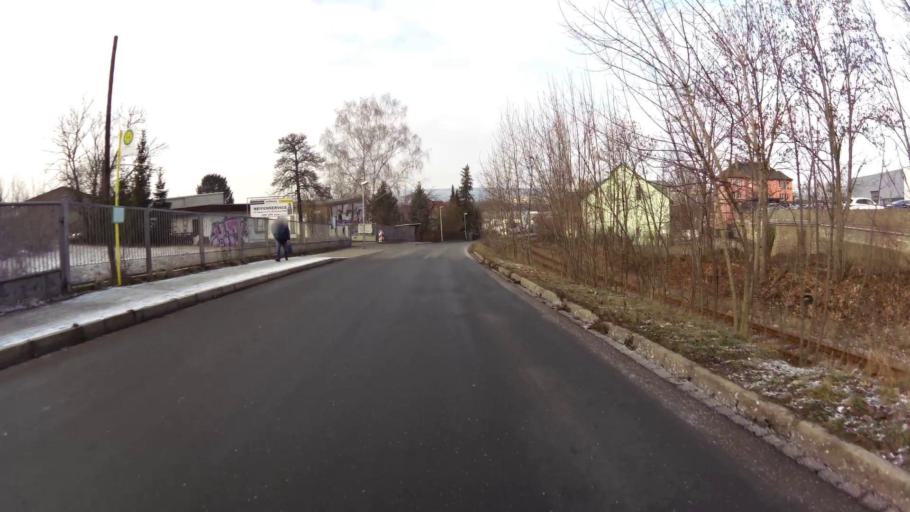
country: DE
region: Thuringia
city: Weimar
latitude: 50.9812
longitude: 11.3088
